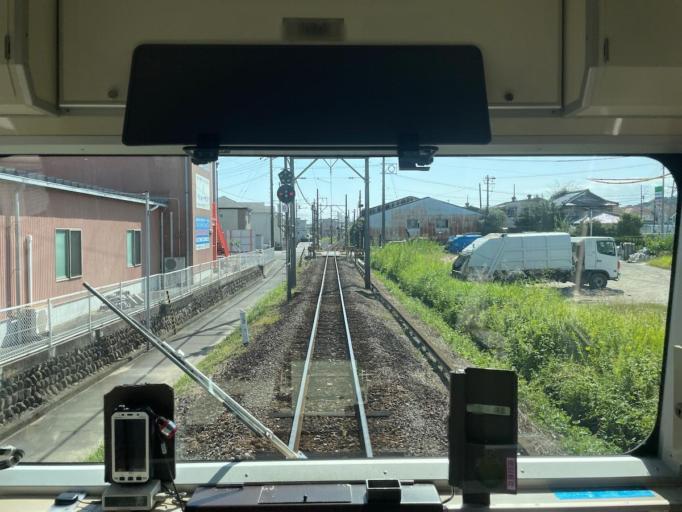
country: JP
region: Mie
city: Yokkaichi
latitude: 34.9424
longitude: 136.5992
